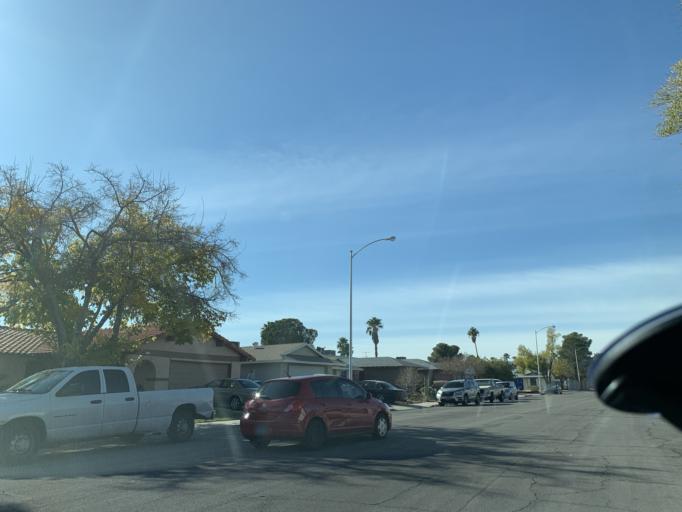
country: US
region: Nevada
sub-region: Clark County
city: Spring Valley
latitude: 36.1046
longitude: -115.2297
